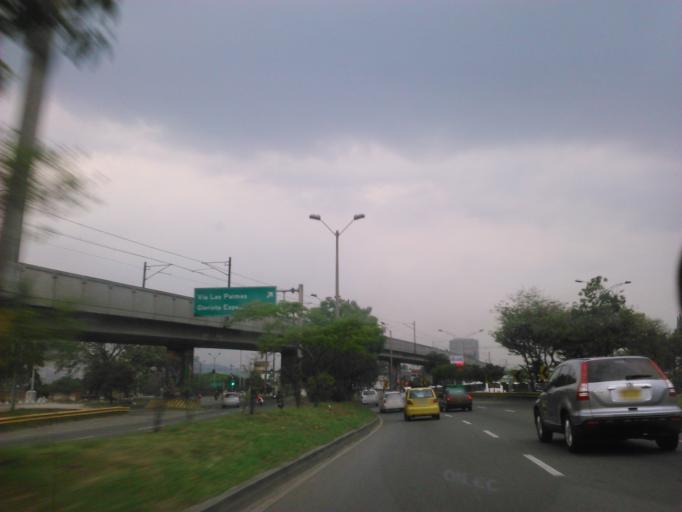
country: CO
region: Antioquia
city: Medellin
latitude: 6.2328
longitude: -75.5750
